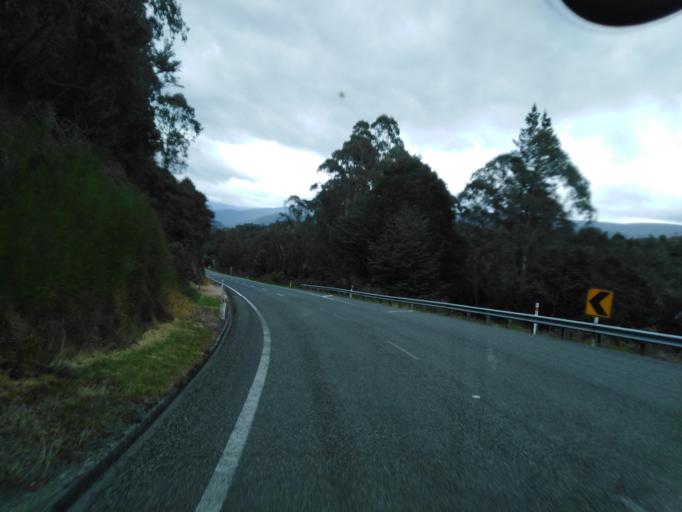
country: NZ
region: Tasman
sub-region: Tasman District
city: Wakefield
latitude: -41.6285
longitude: 172.6990
